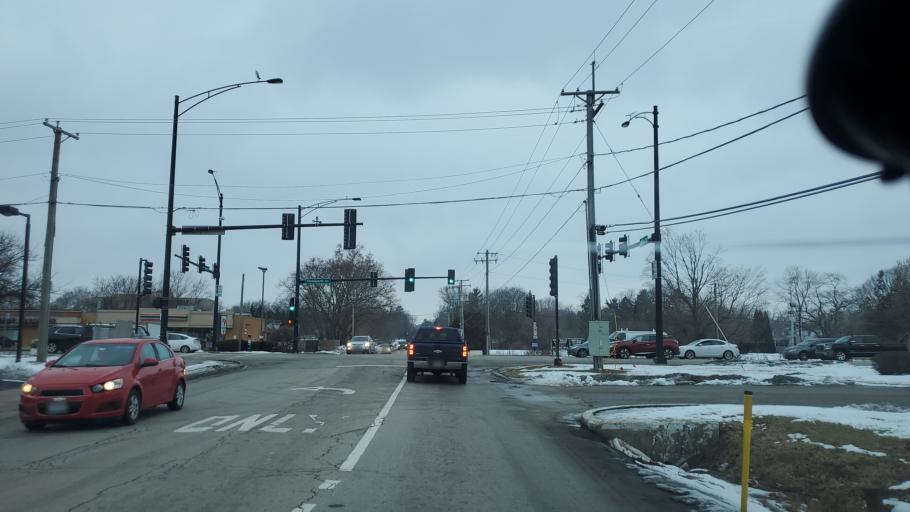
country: US
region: Illinois
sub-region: Kane County
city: North Aurora
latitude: 41.7939
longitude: -88.2814
